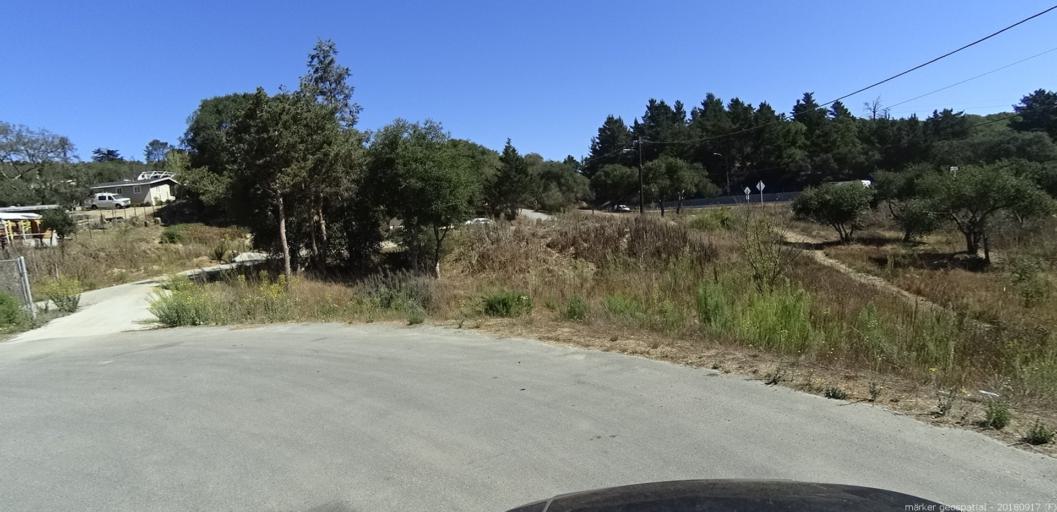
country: US
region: California
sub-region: Monterey County
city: Prunedale
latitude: 36.8220
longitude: -121.6312
